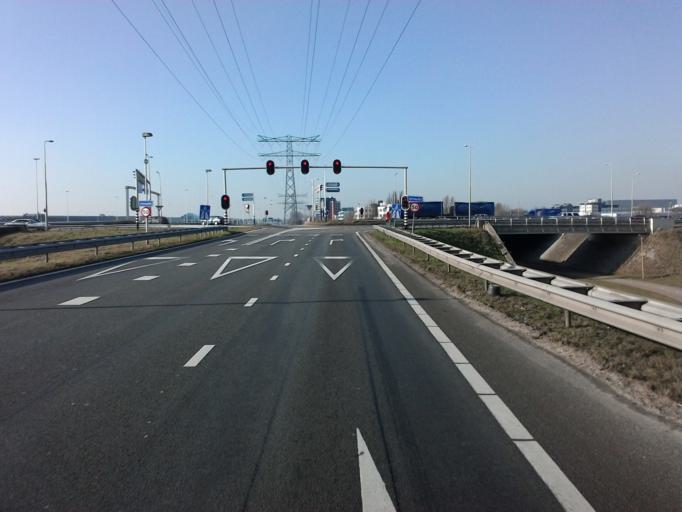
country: NL
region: Utrecht
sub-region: Stichtse Vecht
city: Maarssen
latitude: 52.1101
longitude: 5.0543
